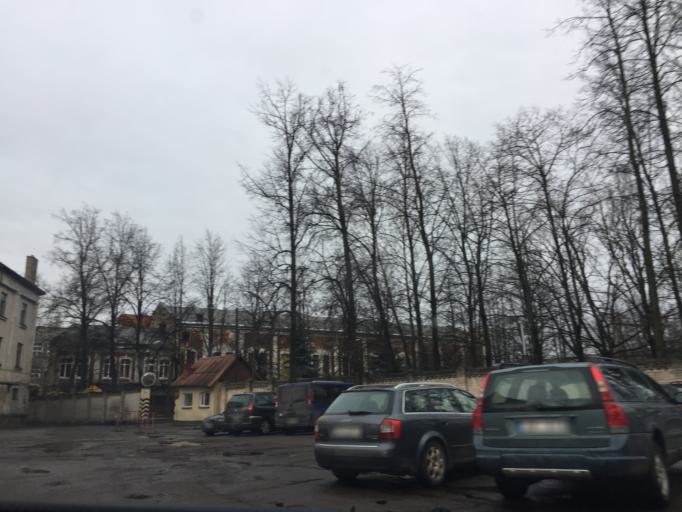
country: LV
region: Riga
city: Riga
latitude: 56.9915
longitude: 24.1211
